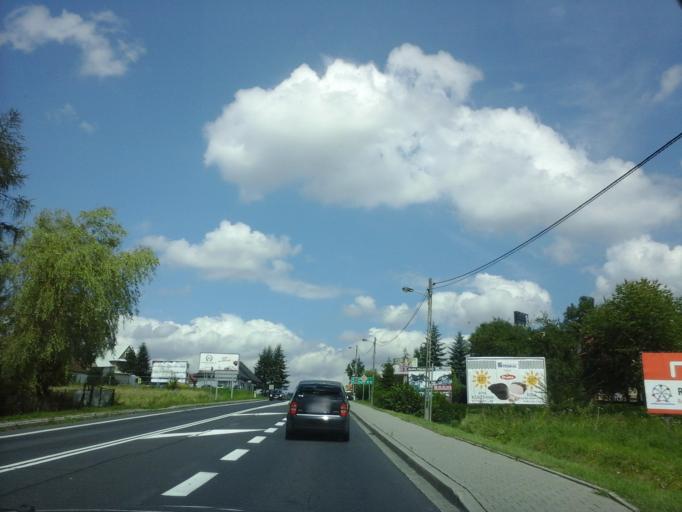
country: PL
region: Lesser Poland Voivodeship
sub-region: Powiat nowotarski
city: Rokiciny
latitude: 49.6066
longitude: 19.9283
